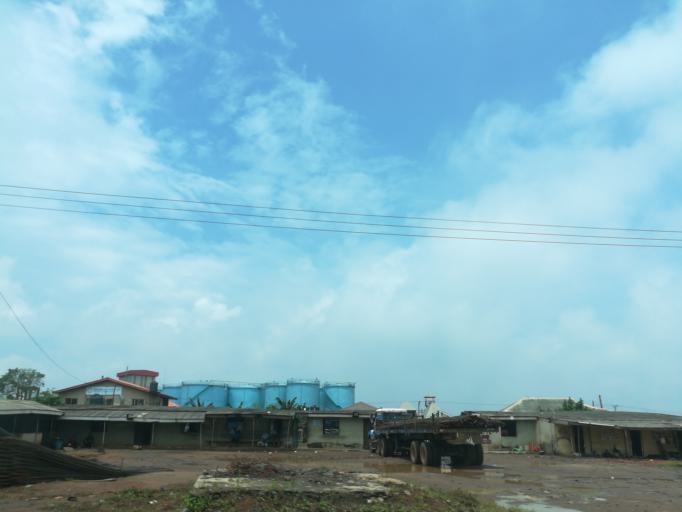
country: NG
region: Lagos
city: Ikorodu
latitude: 6.6677
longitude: 3.5147
